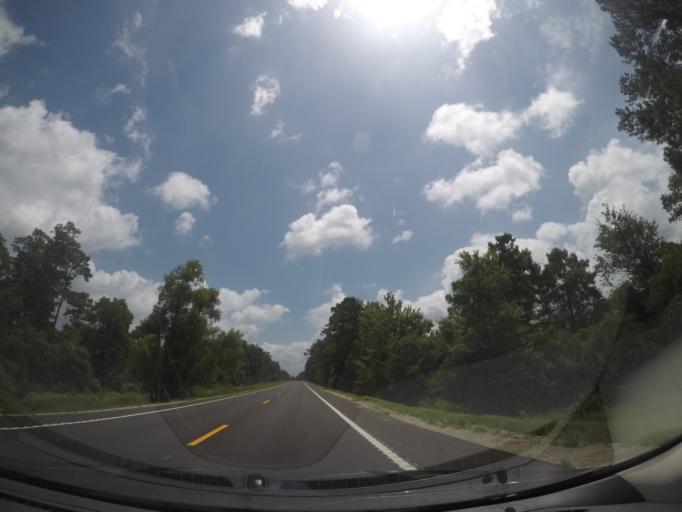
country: US
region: Mississippi
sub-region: Hancock County
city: Pearlington
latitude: 30.2577
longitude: -89.5774
